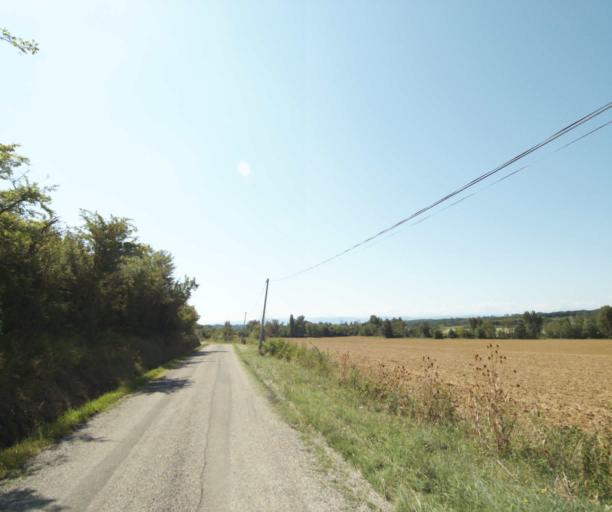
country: FR
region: Midi-Pyrenees
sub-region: Departement de l'Ariege
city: Lezat-sur-Leze
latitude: 43.2559
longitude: 1.3691
